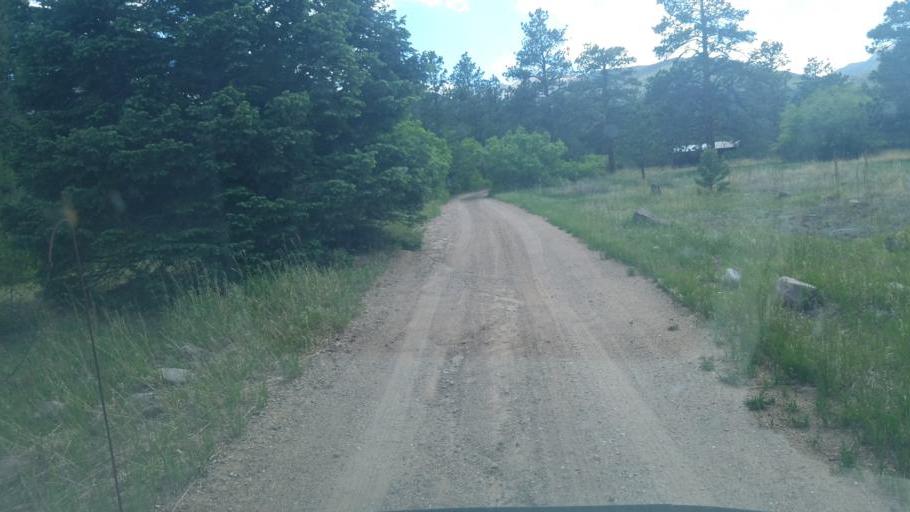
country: US
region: Colorado
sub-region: Custer County
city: Westcliffe
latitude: 38.2208
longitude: -105.6203
